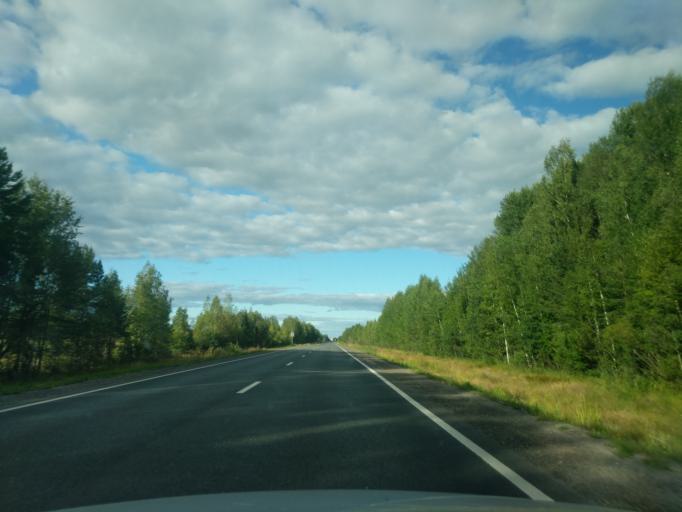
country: RU
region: Kostroma
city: Manturovo
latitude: 58.2271
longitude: 44.6271
